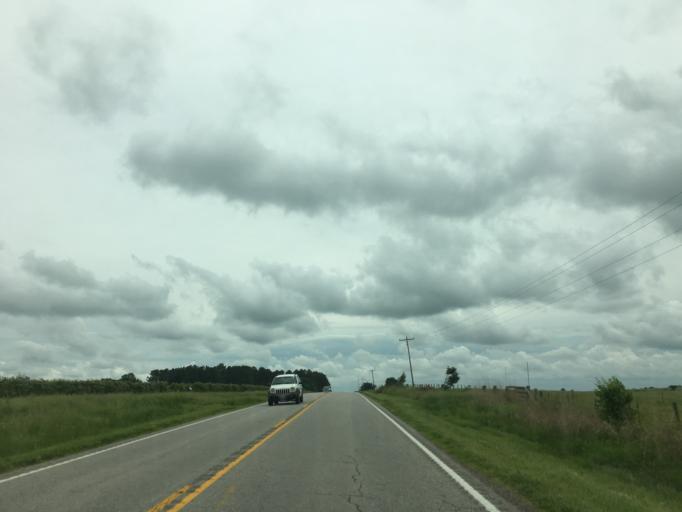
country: US
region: Missouri
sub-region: Gasconade County
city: Owensville
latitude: 38.5102
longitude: -91.4619
